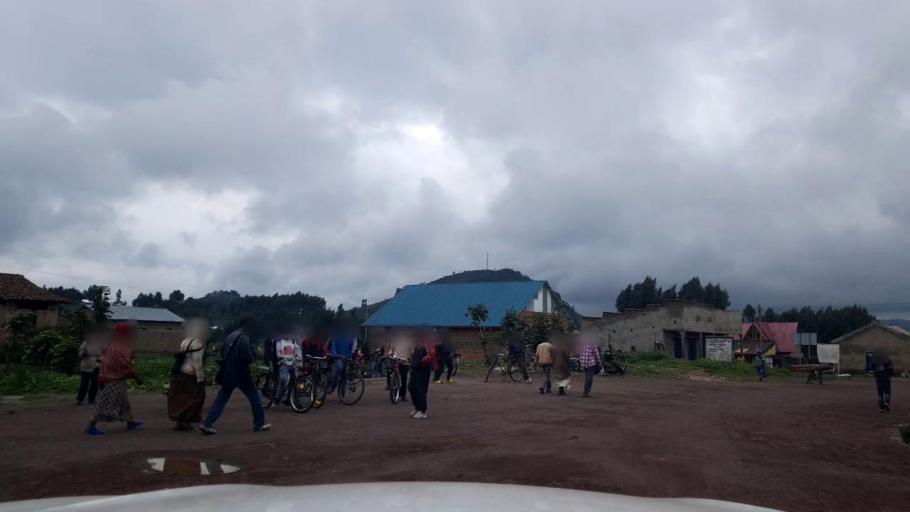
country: RW
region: Northern Province
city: Musanze
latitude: -1.5953
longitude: 29.4525
